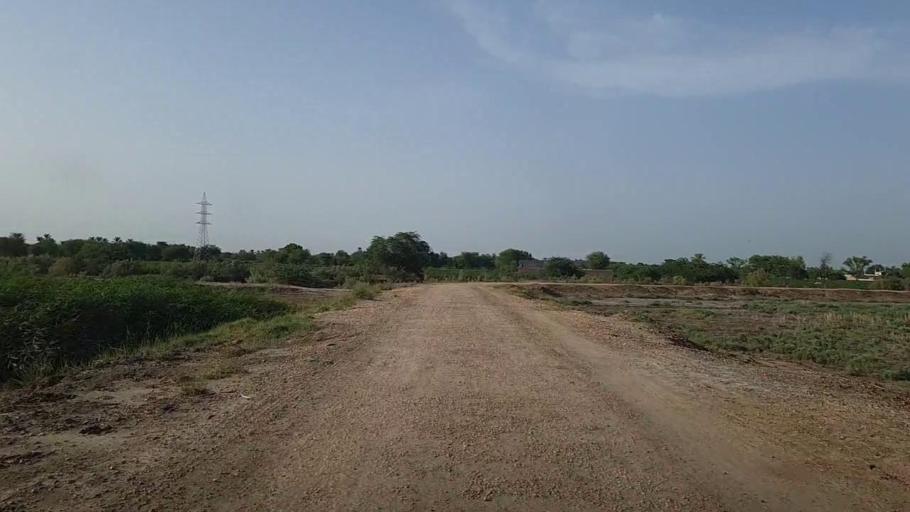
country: PK
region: Sindh
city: Karaundi
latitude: 26.8897
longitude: 68.3060
